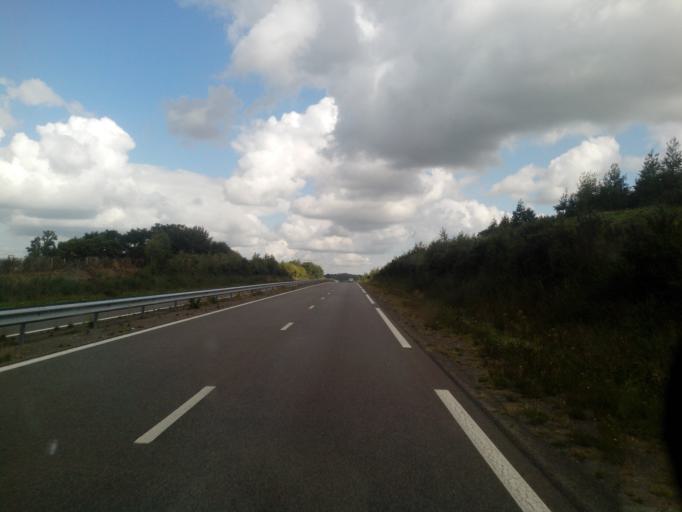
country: FR
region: Brittany
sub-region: Departement d'Ille-et-Vilaine
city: Betton
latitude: 48.1896
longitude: -1.6233
